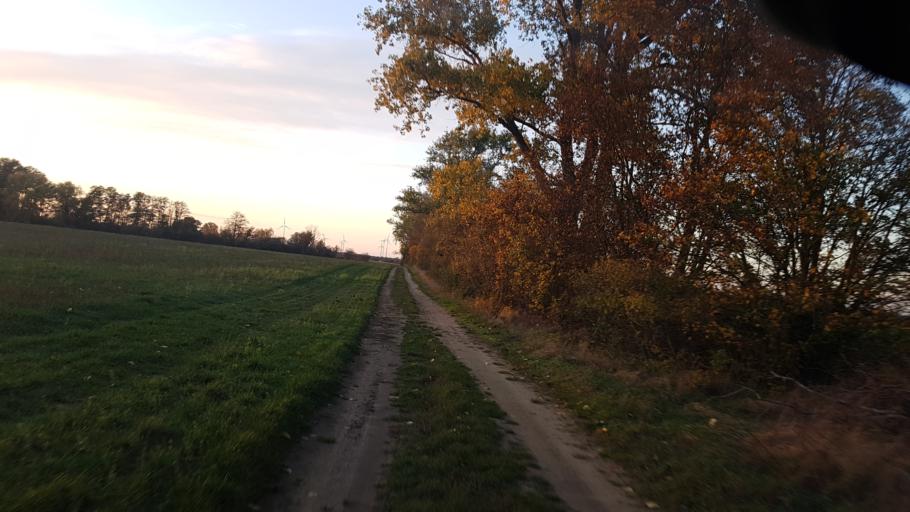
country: DE
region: Brandenburg
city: Muhlberg
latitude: 51.4965
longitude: 13.2741
